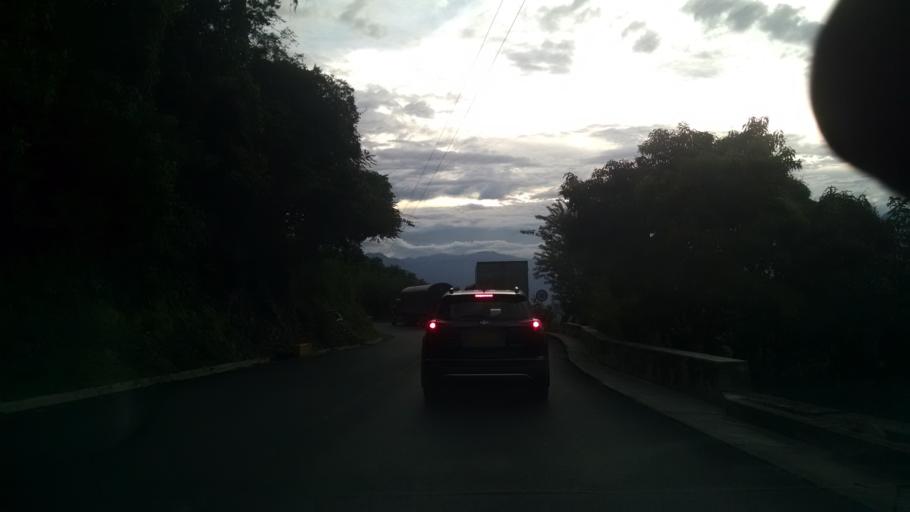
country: CO
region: Antioquia
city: Santa Barbara
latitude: 5.8421
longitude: -75.5775
